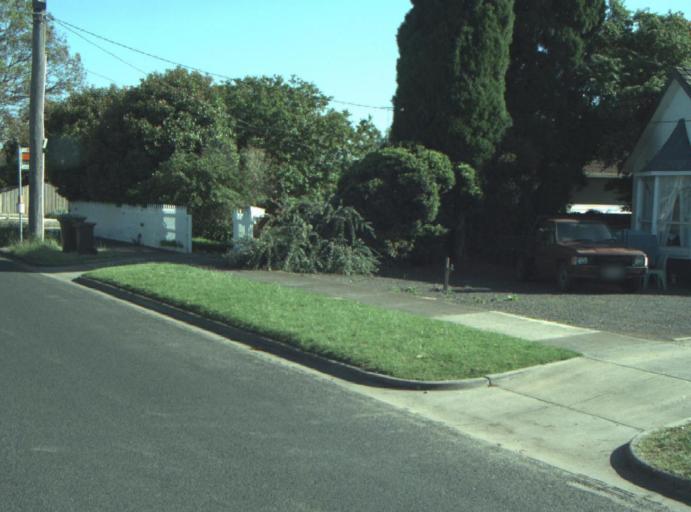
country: AU
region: Victoria
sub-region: Greater Geelong
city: Lara
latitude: -38.0190
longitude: 144.4052
